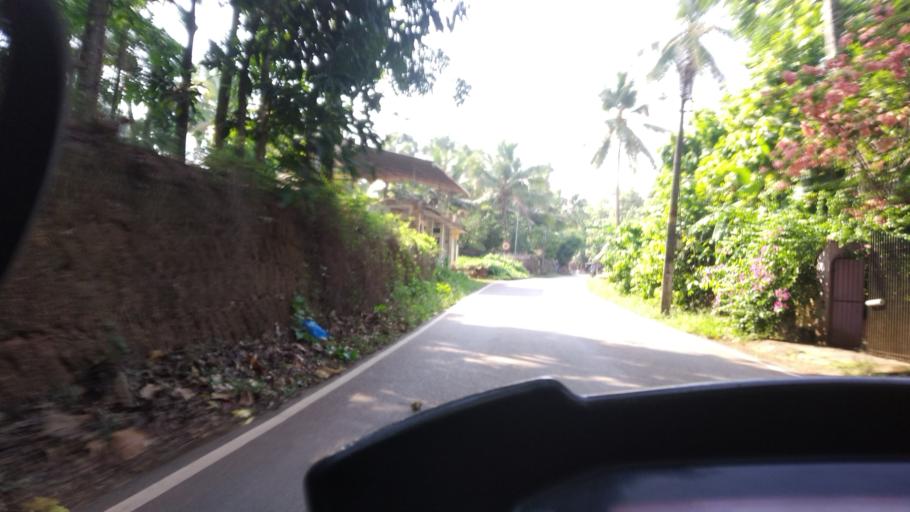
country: IN
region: Kerala
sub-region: Ernakulam
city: Piravam
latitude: 9.8565
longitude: 76.5229
